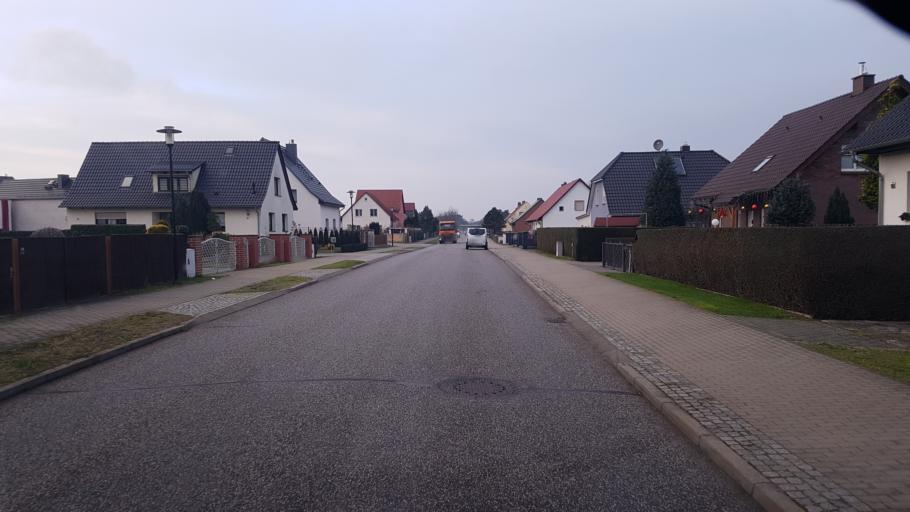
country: DE
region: Brandenburg
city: Vogelsang
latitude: 52.1831
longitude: 14.6616
